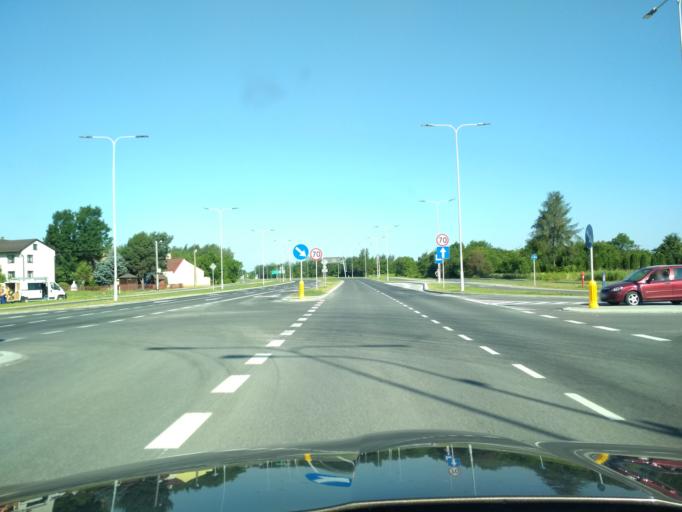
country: PL
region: Subcarpathian Voivodeship
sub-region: Rzeszow
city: Rzeszow
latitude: 50.0646
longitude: 22.0013
